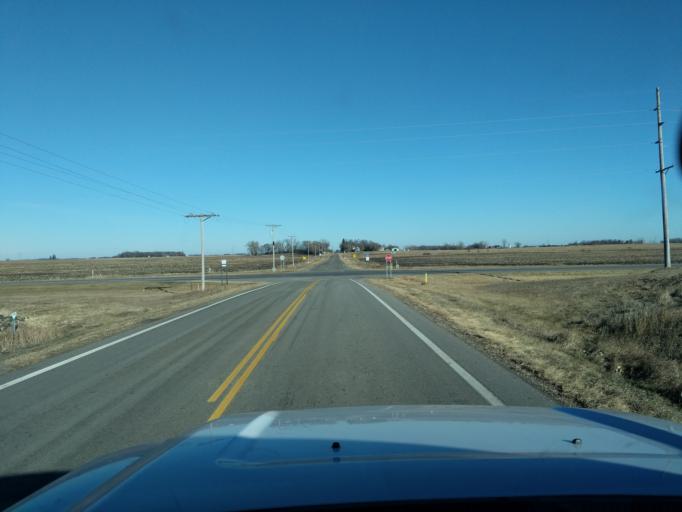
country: US
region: Minnesota
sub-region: Yellow Medicine County
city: Granite Falls
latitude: 44.7883
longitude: -95.4018
